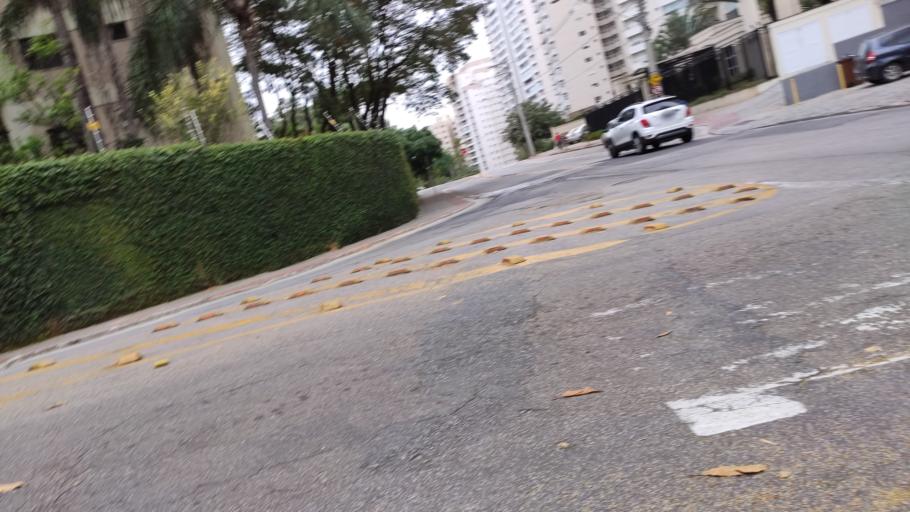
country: BR
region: Sao Paulo
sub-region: Sao Jose Dos Campos
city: Sao Jose dos Campos
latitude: -23.2076
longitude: -45.9019
